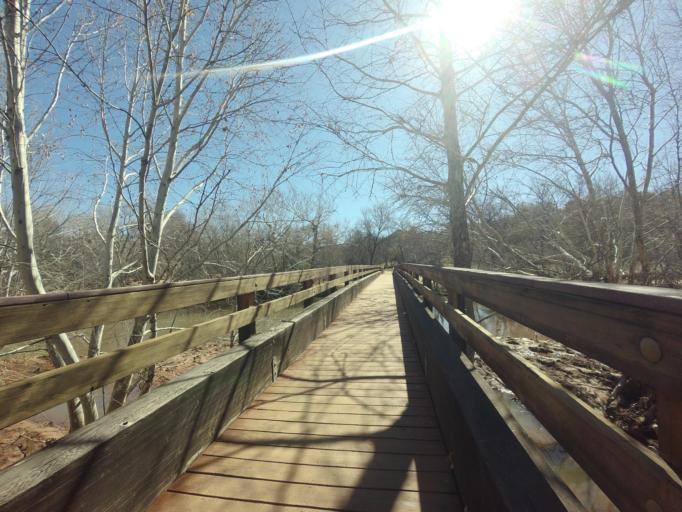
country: US
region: Arizona
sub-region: Yavapai County
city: West Sedona
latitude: 34.8102
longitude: -111.8256
